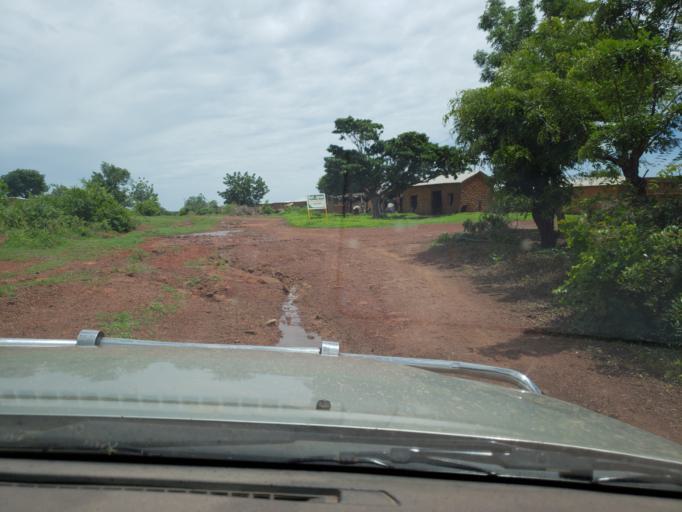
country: ML
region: Sikasso
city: Sikasso
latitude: 11.6758
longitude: -6.1745
